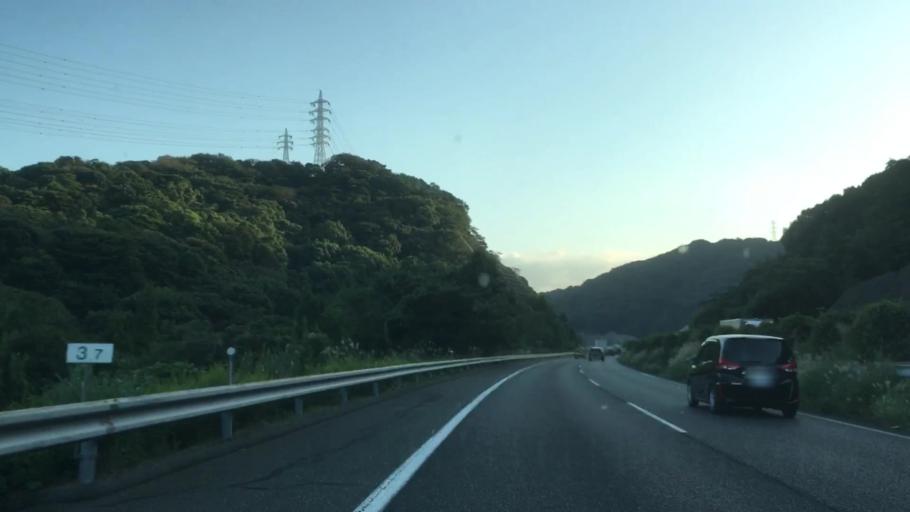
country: JP
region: Yamaguchi
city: Shimonoseki
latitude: 33.8938
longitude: 130.9720
